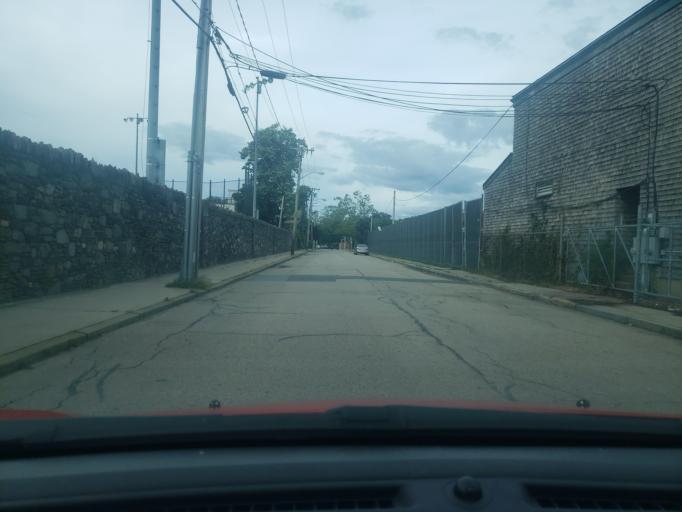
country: US
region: Rhode Island
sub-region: Newport County
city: Newport
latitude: 41.4824
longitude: -71.3059
